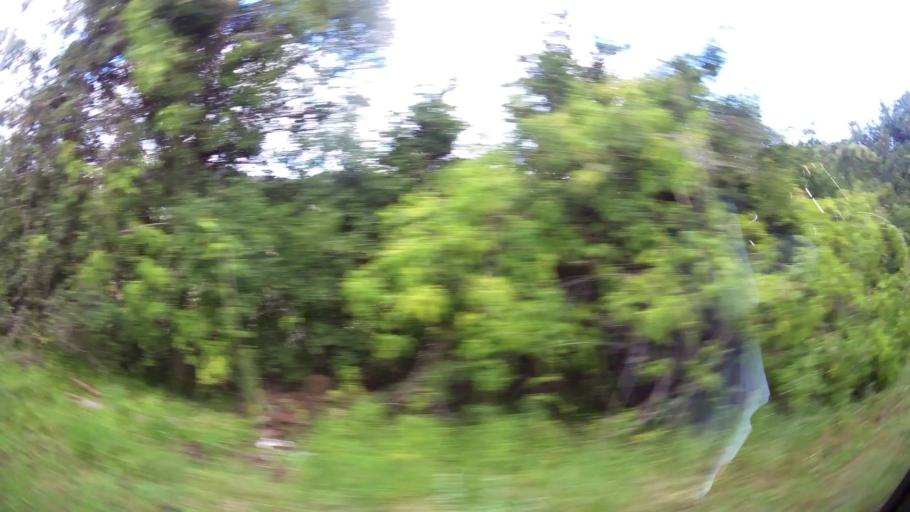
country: ZA
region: Western Cape
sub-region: Eden District Municipality
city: Knysna
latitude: -34.0582
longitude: 23.0837
